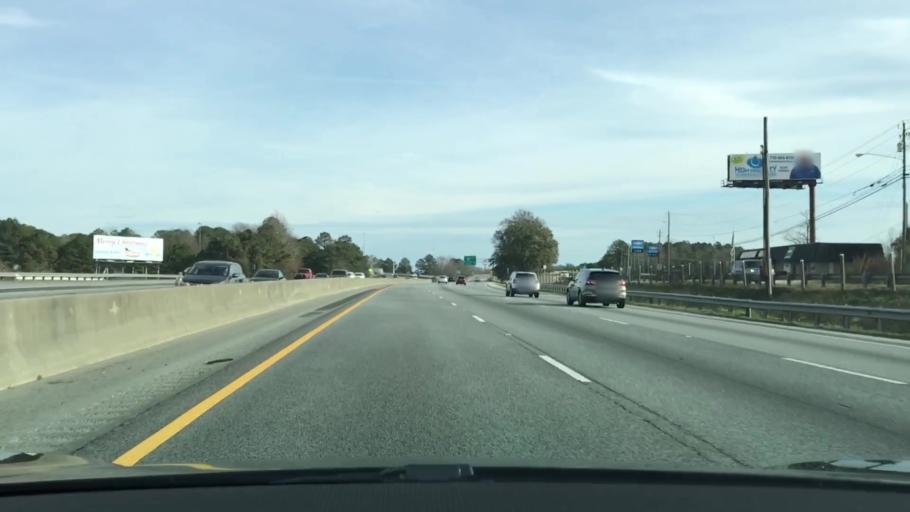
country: US
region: Georgia
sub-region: Newton County
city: Oxford
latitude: 33.6090
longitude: -83.8828
